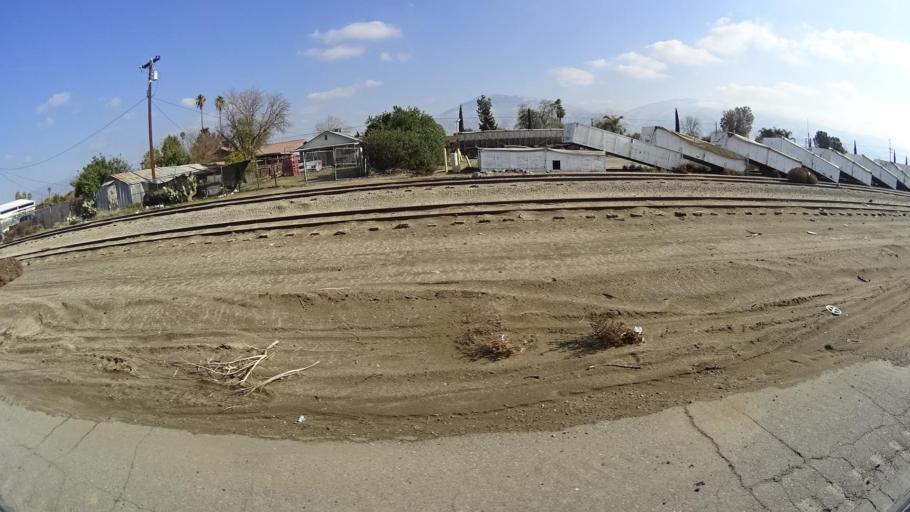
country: US
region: California
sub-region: Kern County
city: Arvin
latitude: 35.2252
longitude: -118.8244
